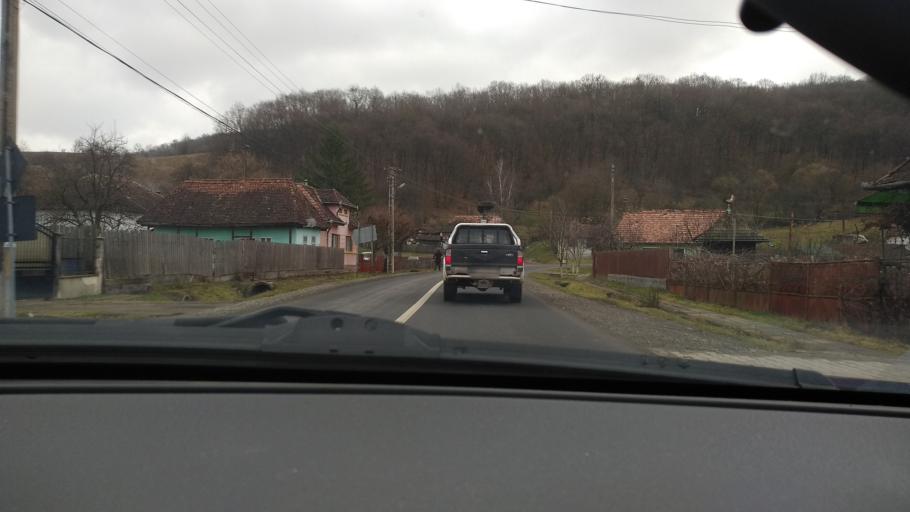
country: RO
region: Mures
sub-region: Comuna Bereni
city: Bereni
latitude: 46.5563
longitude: 24.8677
